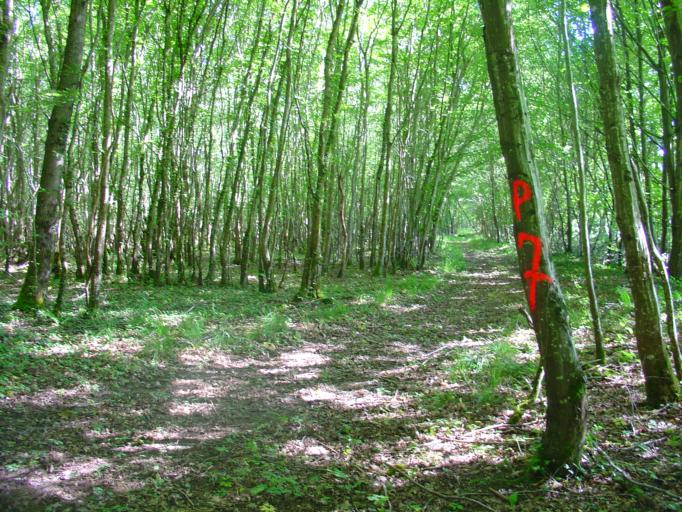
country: FR
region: Lorraine
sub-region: Departement de Meurthe-et-Moselle
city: Toul
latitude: 48.7878
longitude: 5.8839
